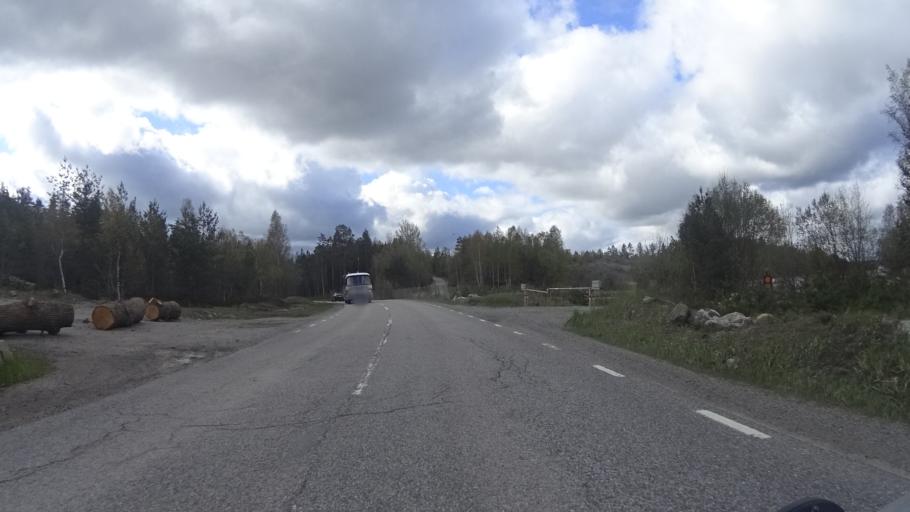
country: SE
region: Stockholm
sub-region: Botkyrka Kommun
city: Tullinge
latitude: 59.1853
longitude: 17.9277
